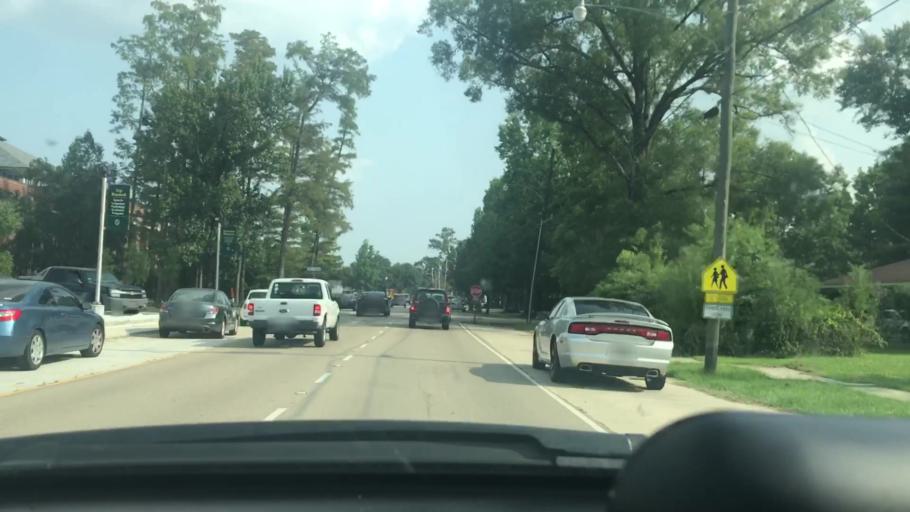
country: US
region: Louisiana
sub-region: Tangipahoa Parish
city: Hammond
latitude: 30.5101
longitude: -90.4642
